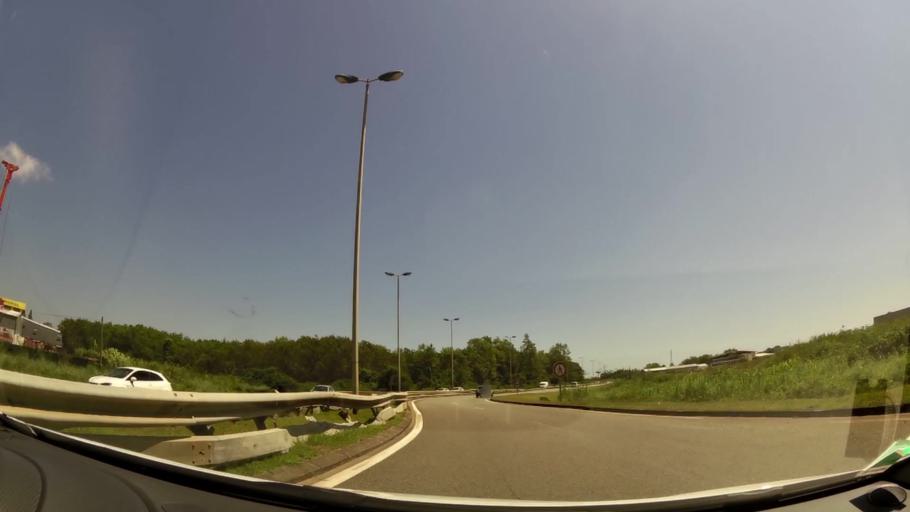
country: GF
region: Guyane
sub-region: Guyane
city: Cayenne
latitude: 4.9219
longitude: -52.3297
